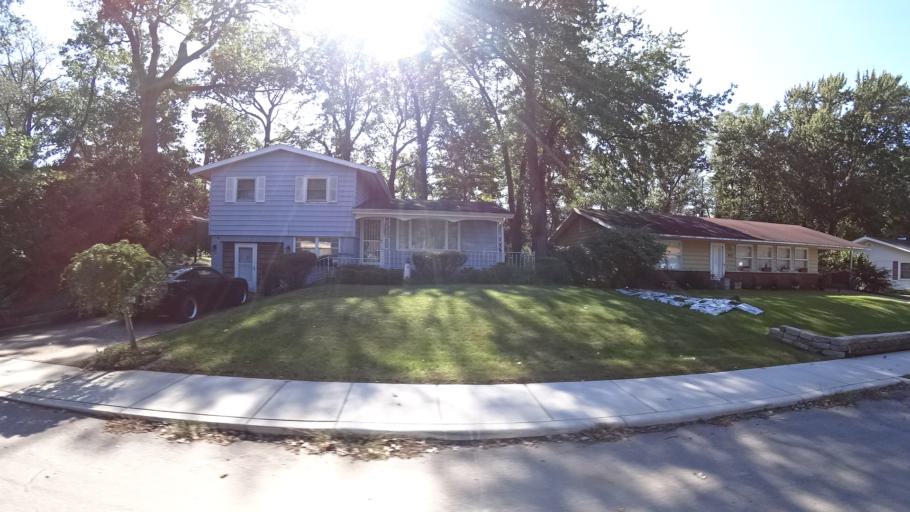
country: US
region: Indiana
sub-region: LaPorte County
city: Michigan City
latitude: 41.7268
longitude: -86.8880
